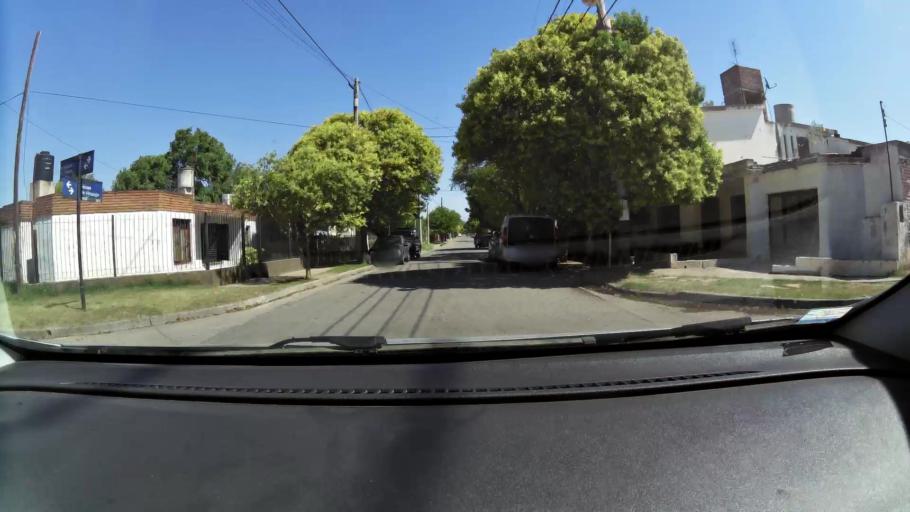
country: AR
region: Cordoba
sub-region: Departamento de Capital
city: Cordoba
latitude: -31.3684
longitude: -64.1365
